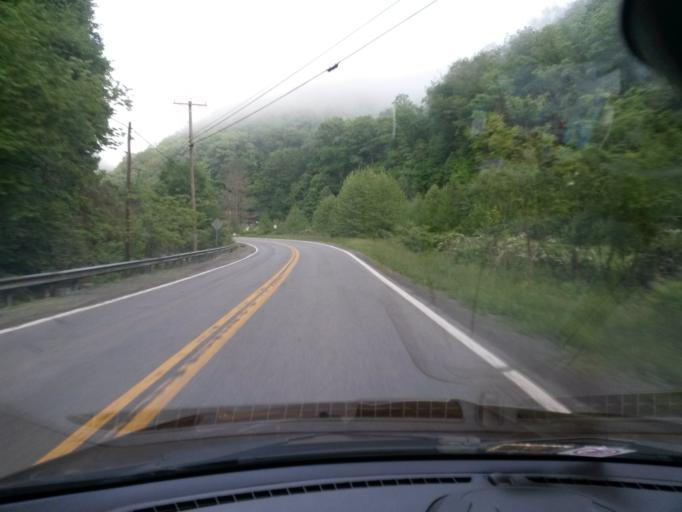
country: US
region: West Virginia
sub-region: McDowell County
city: Welch
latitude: 37.4485
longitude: -81.5468
